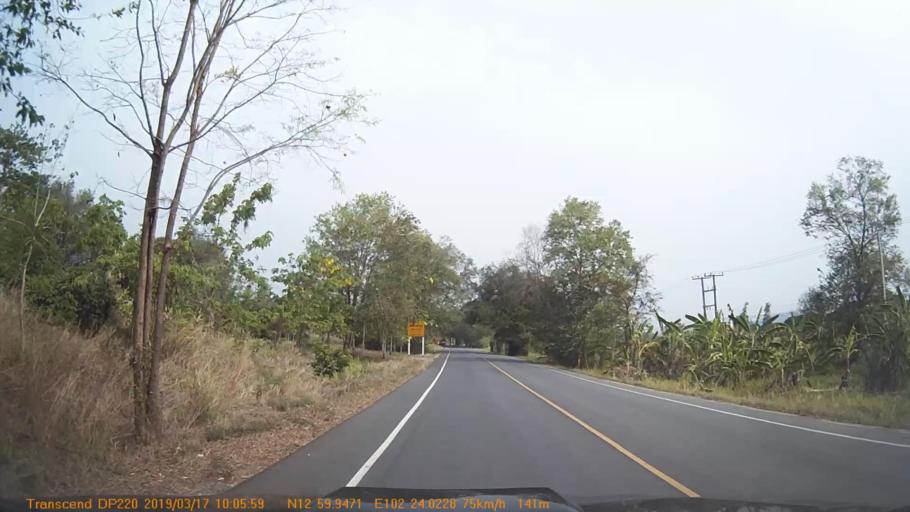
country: TH
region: Chanthaburi
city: Pong Nam Ron
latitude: 13.0008
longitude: 102.4004
